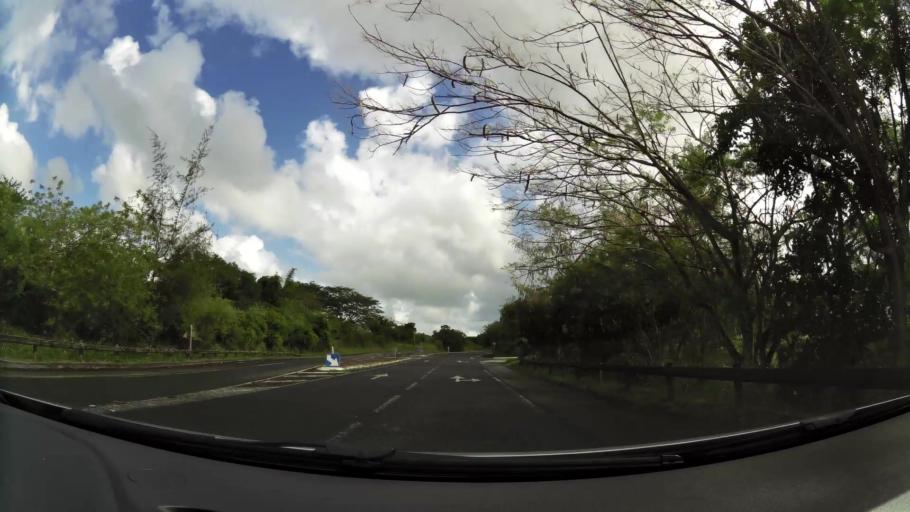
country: MQ
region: Martinique
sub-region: Martinique
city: Sainte-Luce
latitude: 14.4950
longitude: -60.9860
